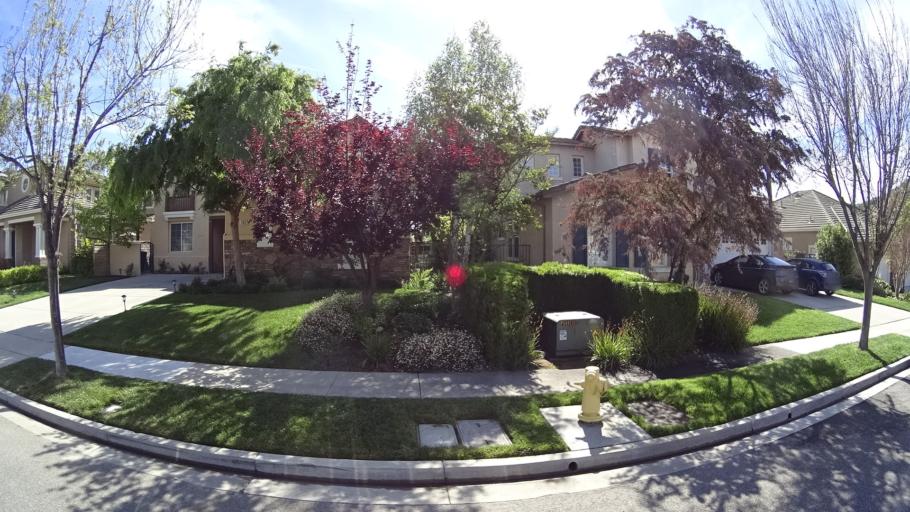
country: US
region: California
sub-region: Ventura County
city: Casa Conejo
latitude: 34.1731
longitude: -118.9821
